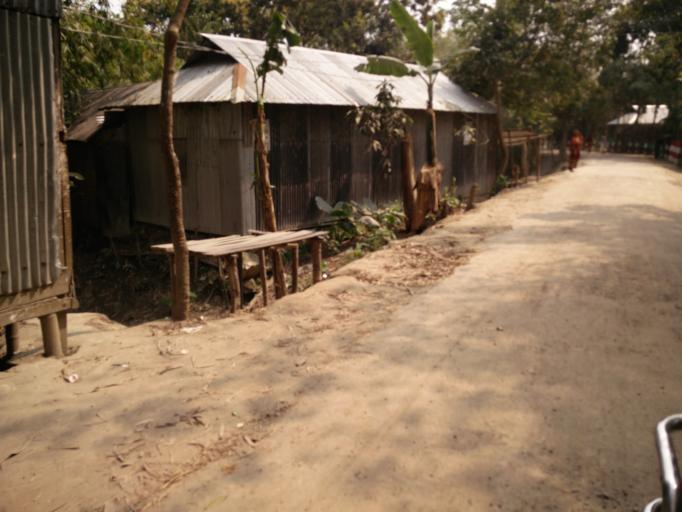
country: BD
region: Rangpur Division
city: Nageswari
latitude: 25.8907
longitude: 89.7194
